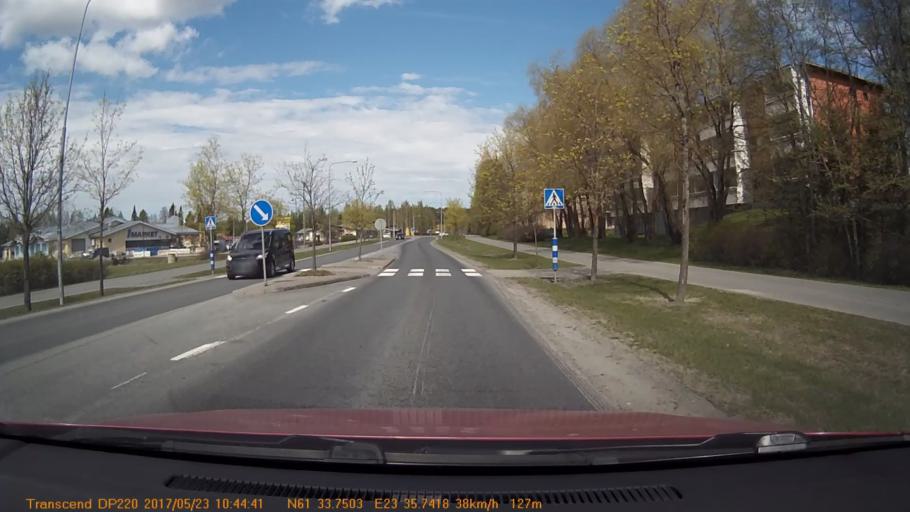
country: FI
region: Pirkanmaa
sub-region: Tampere
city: Yloejaervi
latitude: 61.5624
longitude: 23.5957
